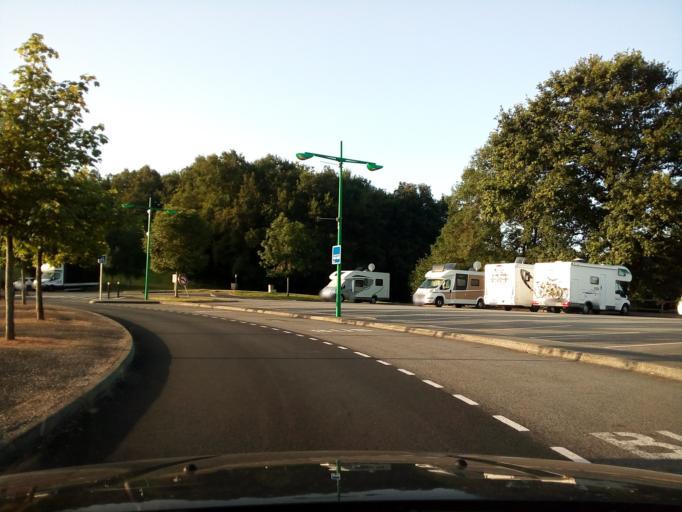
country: FR
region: Limousin
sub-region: Departement de la Creuse
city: Gueret
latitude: 46.1823
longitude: 1.8479
